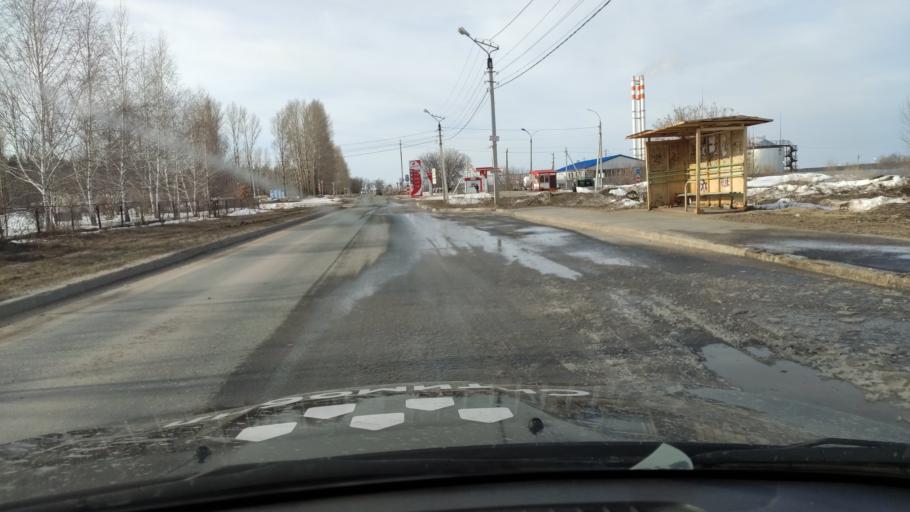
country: RU
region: Samara
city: Povolzhskiy
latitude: 53.5896
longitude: 49.7561
